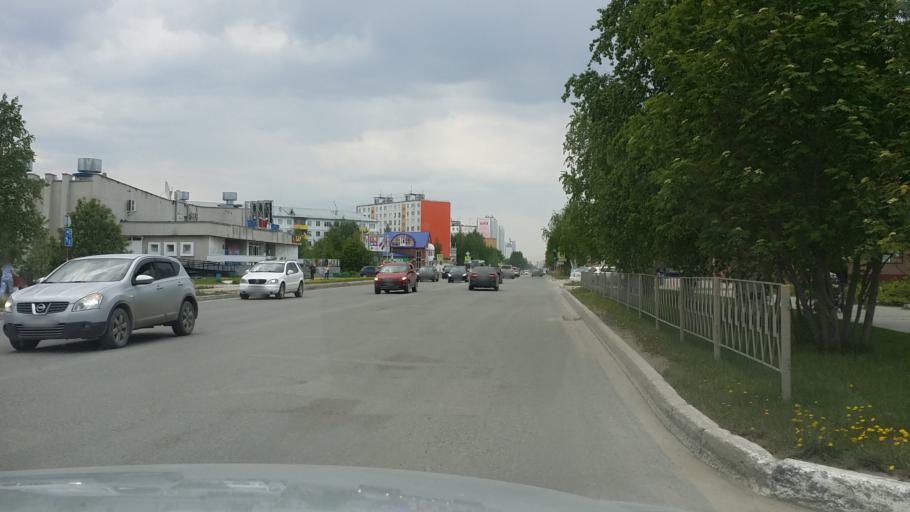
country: RU
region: Khanty-Mansiyskiy Avtonomnyy Okrug
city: Nizhnevartovsk
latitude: 60.9361
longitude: 76.6061
